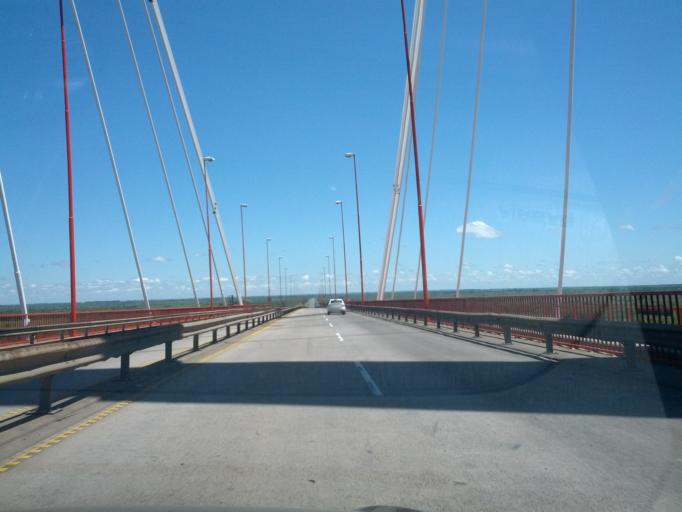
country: AR
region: Buenos Aires
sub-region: Partido de Zarate
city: Zarate
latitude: -33.9108
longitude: -58.8863
